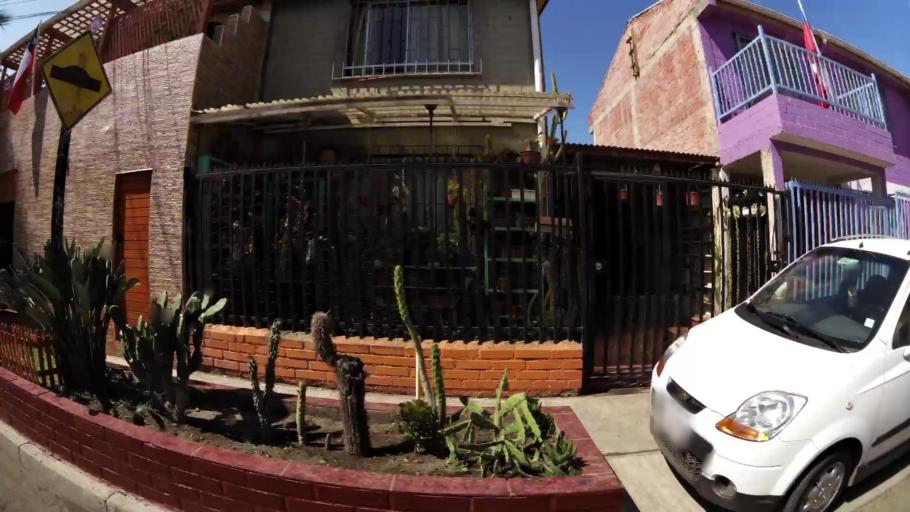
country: CL
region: Santiago Metropolitan
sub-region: Provincia de Santiago
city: Lo Prado
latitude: -33.3519
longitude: -70.7182
